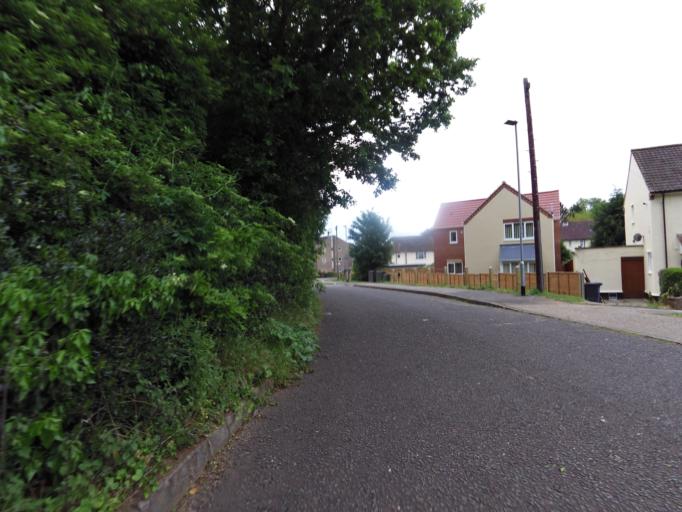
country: GB
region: England
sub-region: Suffolk
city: Ipswich
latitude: 52.0447
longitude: 1.1466
